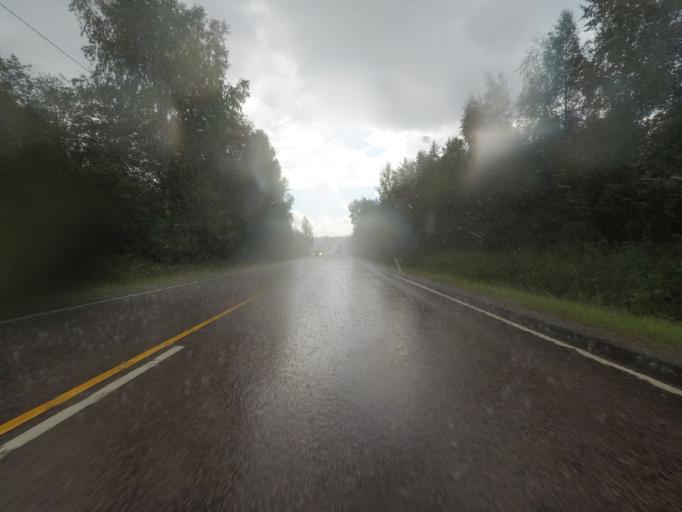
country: FI
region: Central Finland
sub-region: Joutsa
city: Leivonmaeki
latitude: 61.9172
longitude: 26.1168
